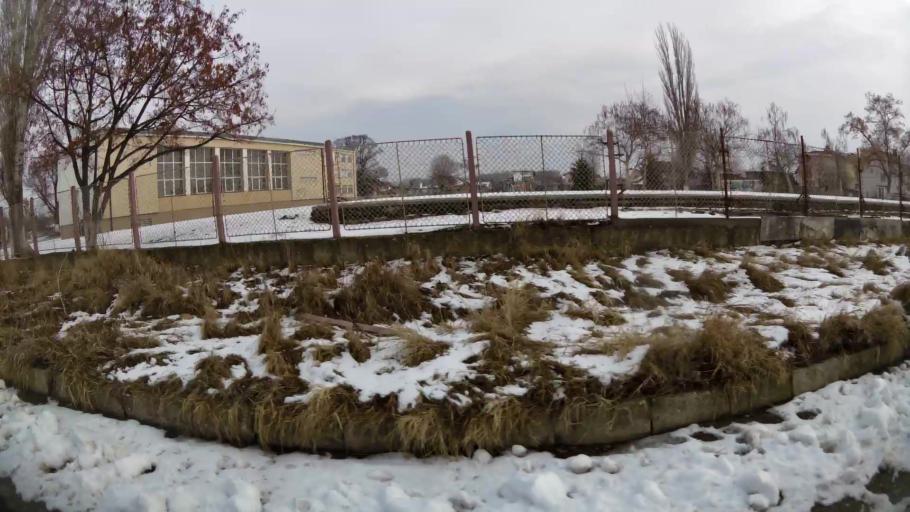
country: BG
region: Sofia-Capital
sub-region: Stolichna Obshtina
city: Sofia
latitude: 42.7110
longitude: 23.4140
